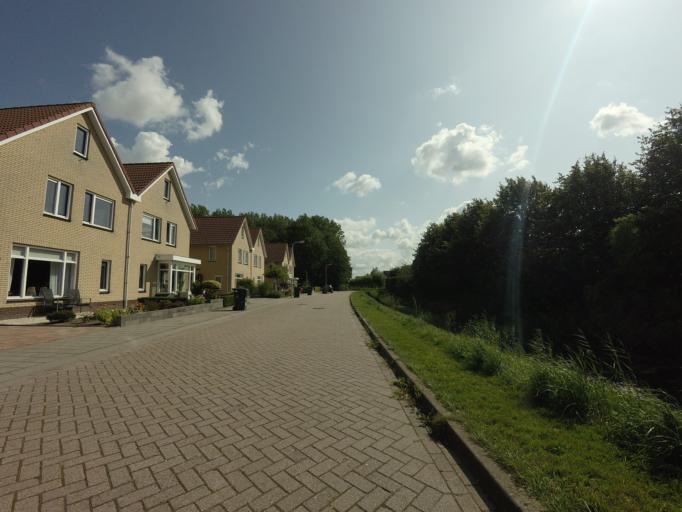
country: NL
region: Friesland
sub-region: Gemeente Het Bildt
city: Sint Annaparochie
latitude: 53.2811
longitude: 5.6598
